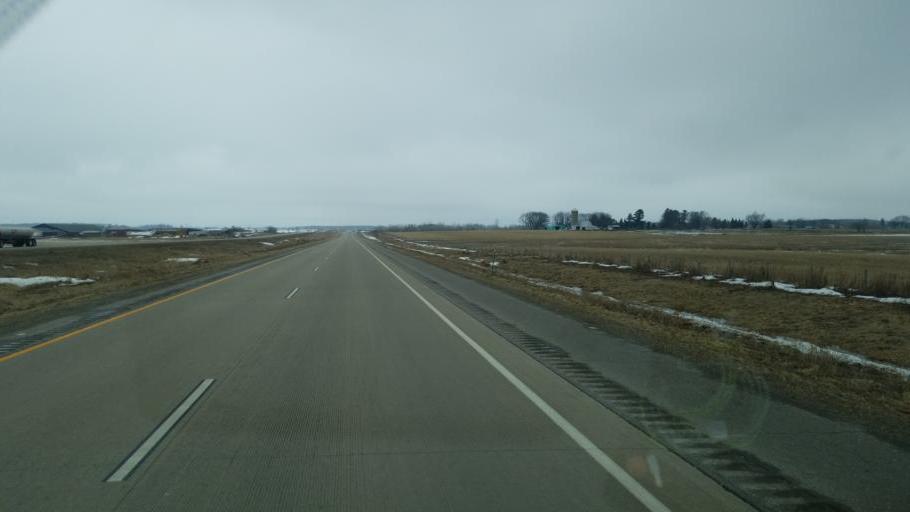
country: US
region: Wisconsin
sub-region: Wood County
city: Marshfield
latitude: 44.6204
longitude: -89.9947
